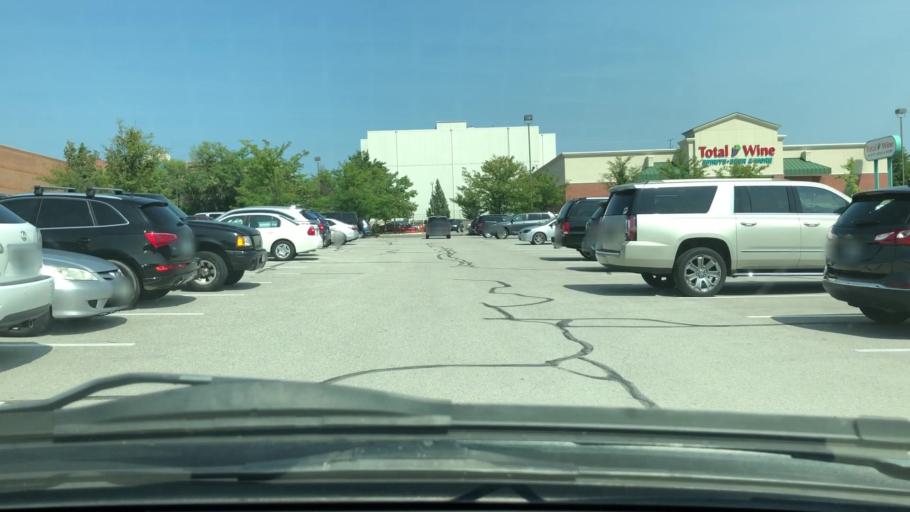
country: US
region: Missouri
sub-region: Saint Louis County
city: Brentwood
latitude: 38.6263
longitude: -90.3424
